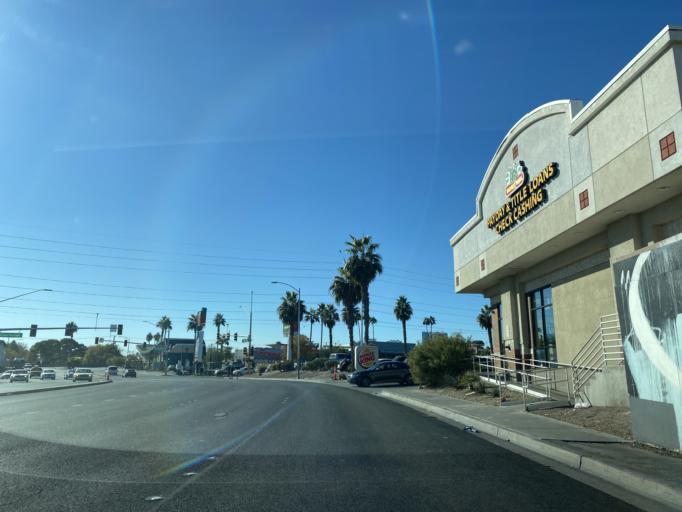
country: US
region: Nevada
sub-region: Clark County
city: Las Vegas
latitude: 36.1597
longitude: -115.1366
